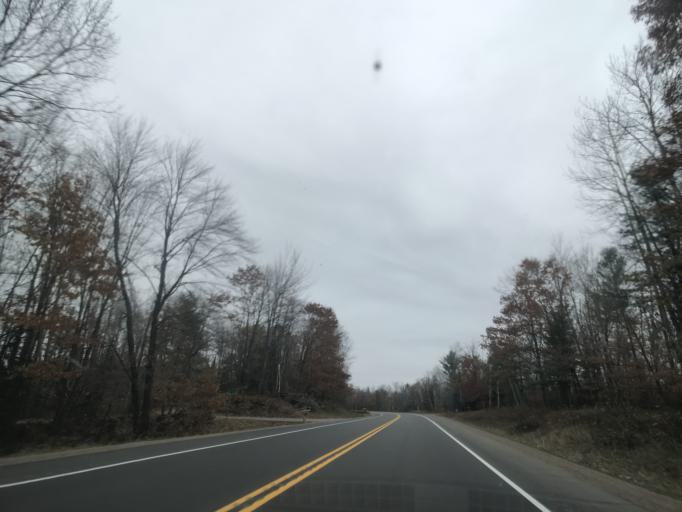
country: US
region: Wisconsin
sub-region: Menominee County
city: Legend Lake
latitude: 45.2697
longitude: -88.5095
